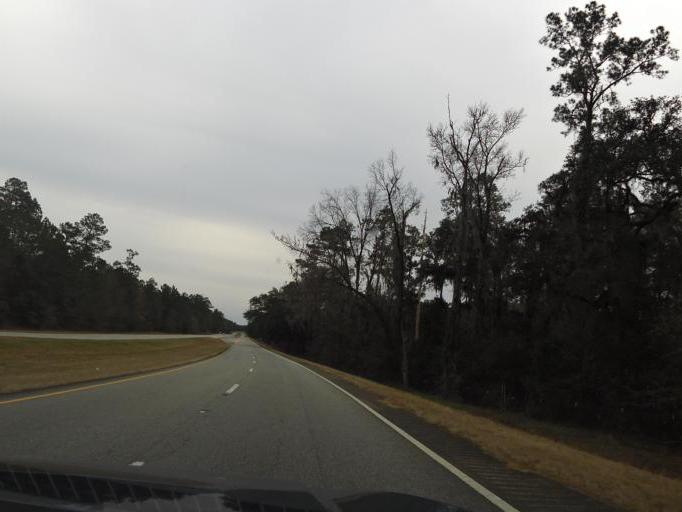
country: US
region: Florida
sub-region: Jefferson County
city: Monticello
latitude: 30.6753
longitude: -83.8866
